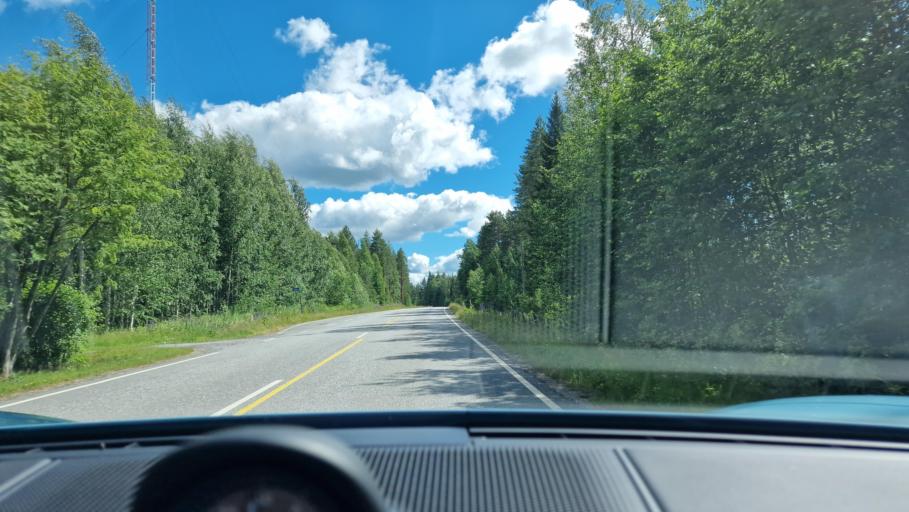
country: FI
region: Southern Ostrobothnia
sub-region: Jaerviseutu
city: Soini
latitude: 62.8211
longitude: 24.3475
